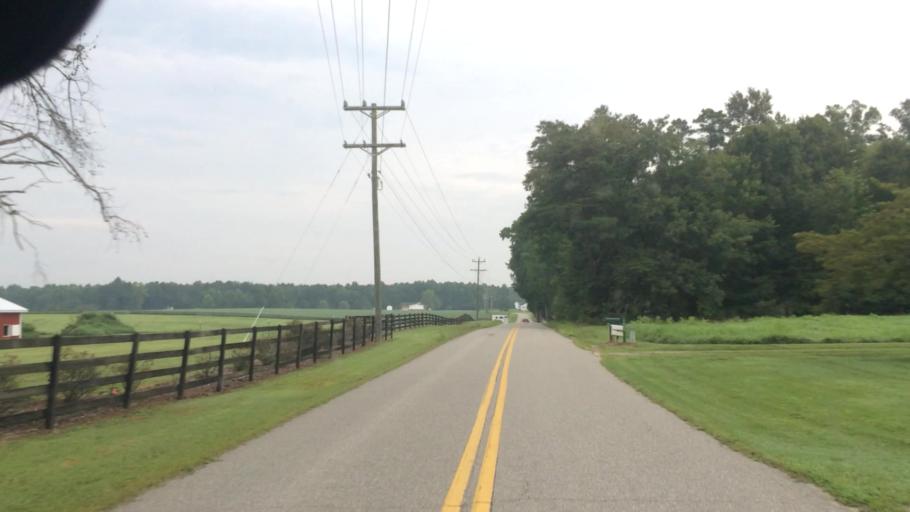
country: US
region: Virginia
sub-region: King William County
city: West Point
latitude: 37.5680
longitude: -76.7068
